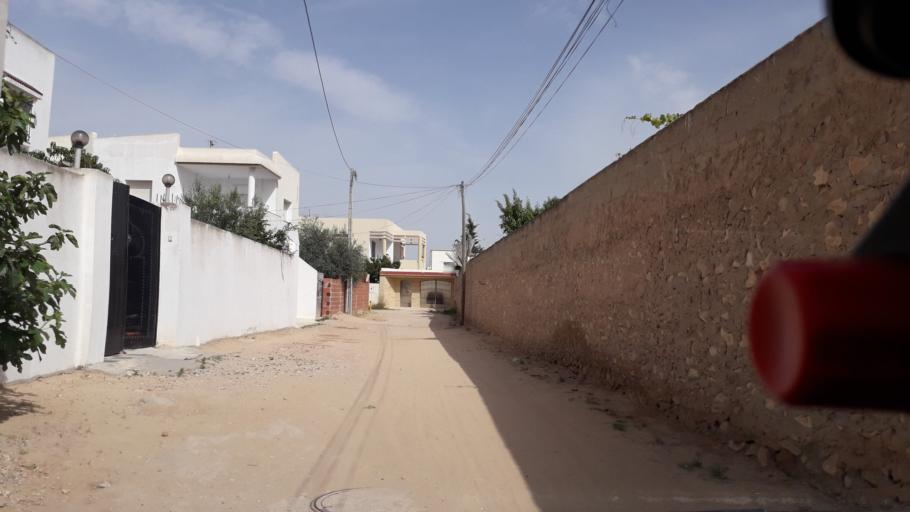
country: TN
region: Safaqis
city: Al Qarmadah
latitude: 34.7975
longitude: 10.7738
